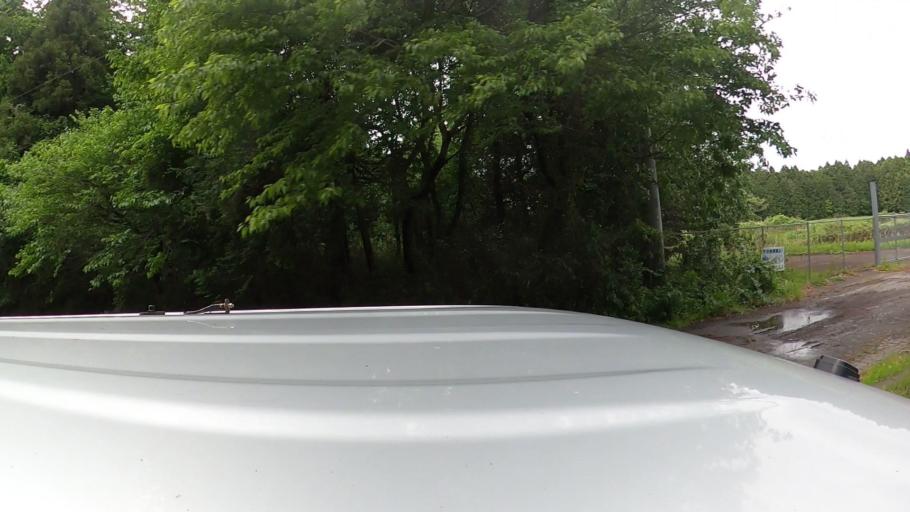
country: JP
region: Ibaraki
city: Edosaki
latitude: 35.9966
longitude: 140.2701
